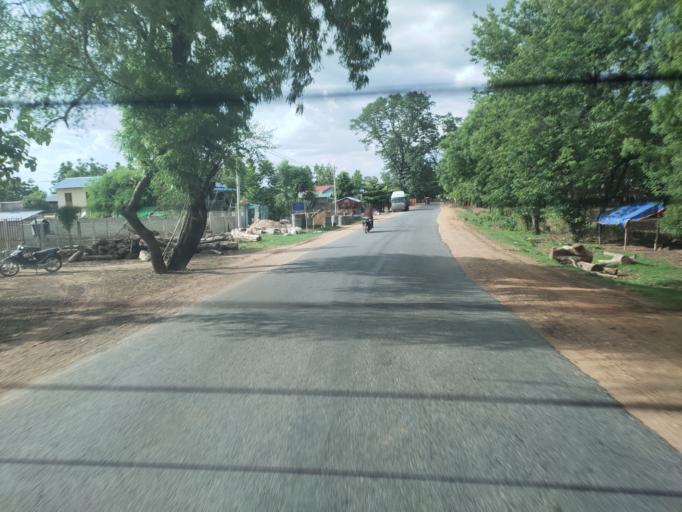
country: MM
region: Magway
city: Magway
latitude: 19.9929
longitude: 94.9883
